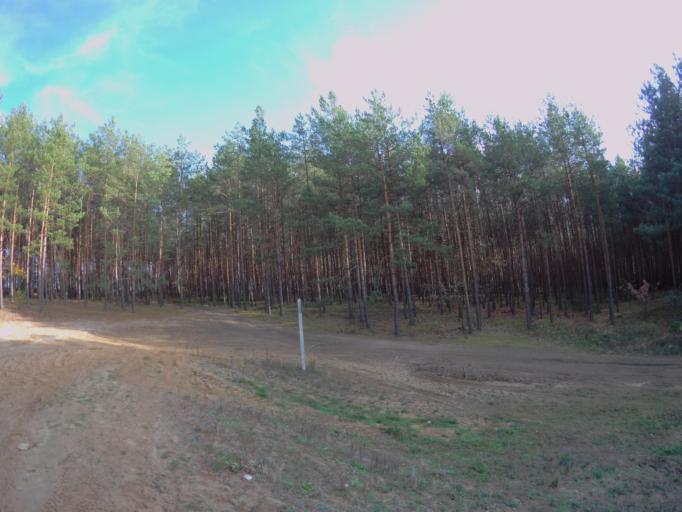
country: PL
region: Subcarpathian Voivodeship
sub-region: Powiat kolbuszowski
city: Lipnica
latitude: 50.3364
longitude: 21.9338
